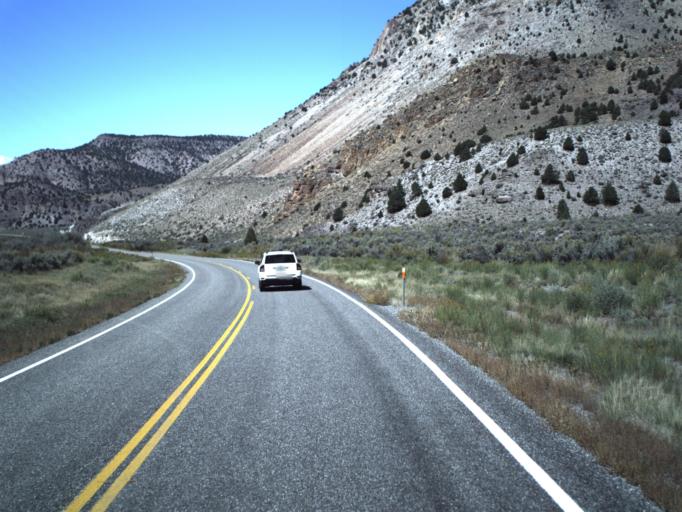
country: US
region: Utah
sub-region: Piute County
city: Junction
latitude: 38.1819
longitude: -112.0803
